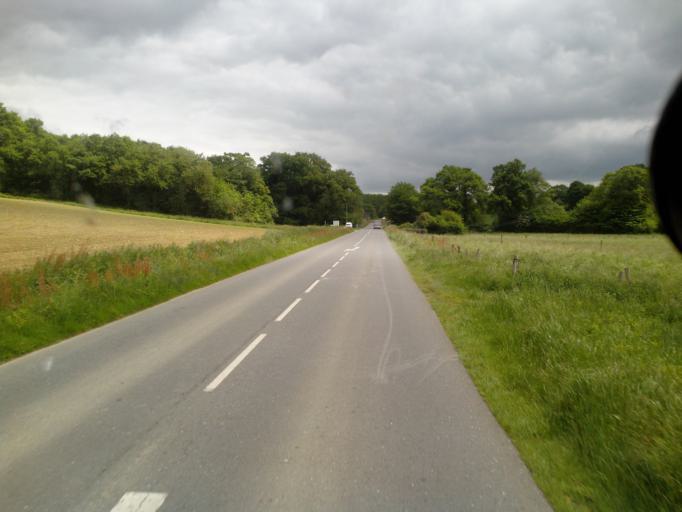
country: FR
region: Brittany
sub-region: Departement d'Ille-et-Vilaine
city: Chasne-sur-Illet
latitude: 48.2479
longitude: -1.5773
